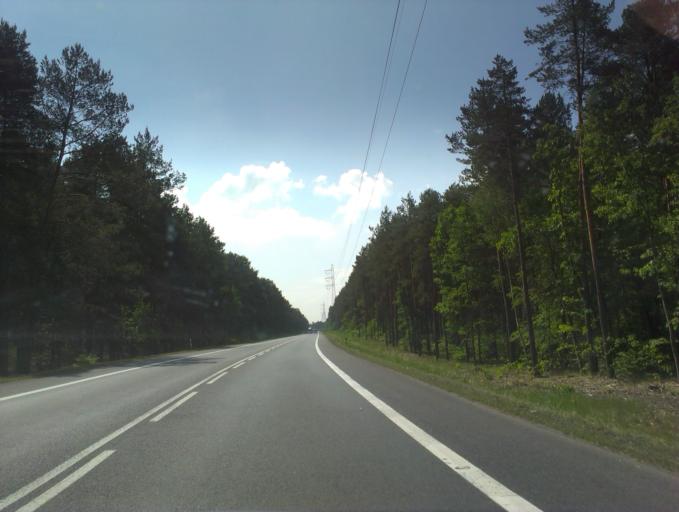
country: PL
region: Greater Poland Voivodeship
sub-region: Powiat pilski
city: Pila
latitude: 53.1608
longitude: 16.7867
